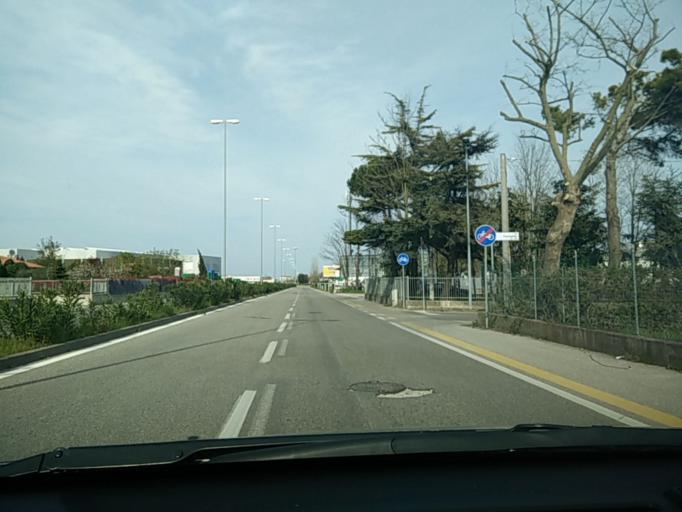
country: IT
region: Emilia-Romagna
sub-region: Provincia di Rimini
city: Santa Giustina
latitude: 44.0756
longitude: 12.5201
